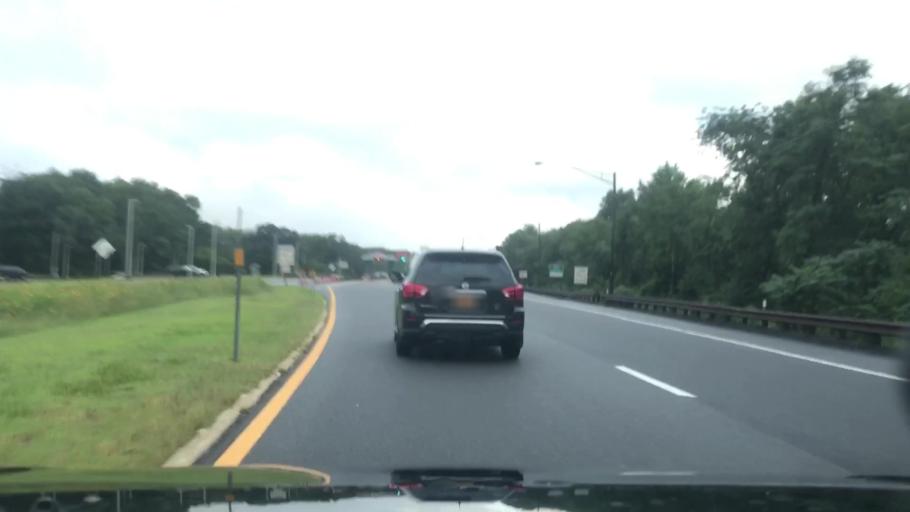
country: US
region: New Jersey
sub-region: Monmouth County
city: Tinton Falls
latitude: 40.2858
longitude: -74.0817
